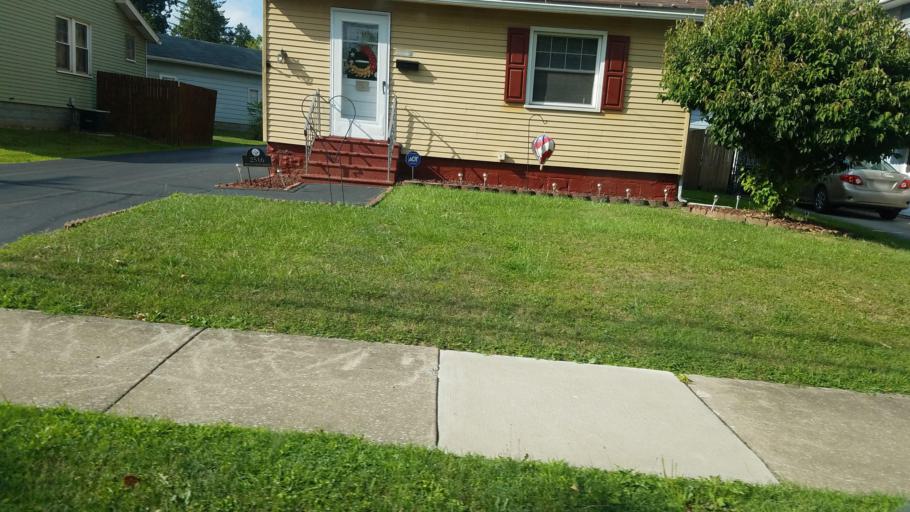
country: US
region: Ohio
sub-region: Mahoning County
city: Struthers
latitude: 41.0616
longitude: -80.6102
